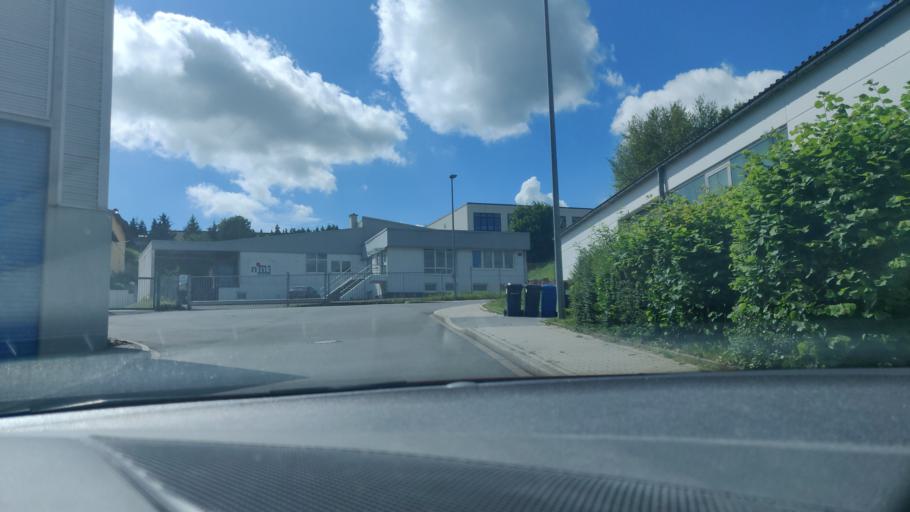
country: DE
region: North Rhine-Westphalia
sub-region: Regierungsbezirk Dusseldorf
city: Heiligenhaus
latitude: 51.3351
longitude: 6.9989
